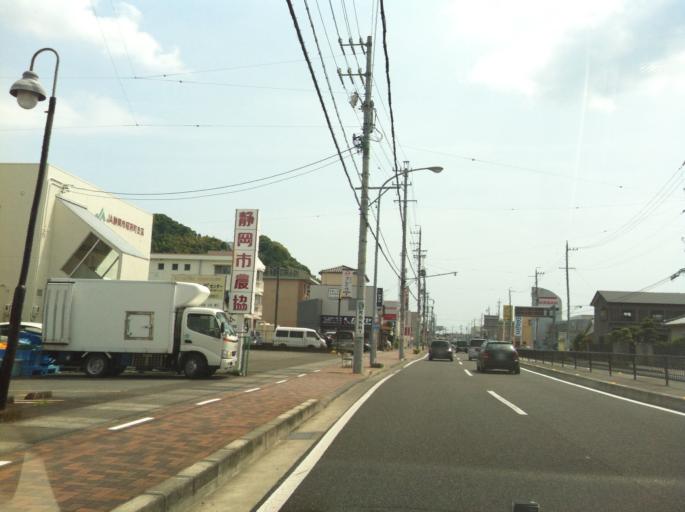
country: JP
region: Shizuoka
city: Shizuoka-shi
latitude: 34.9998
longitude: 138.3704
